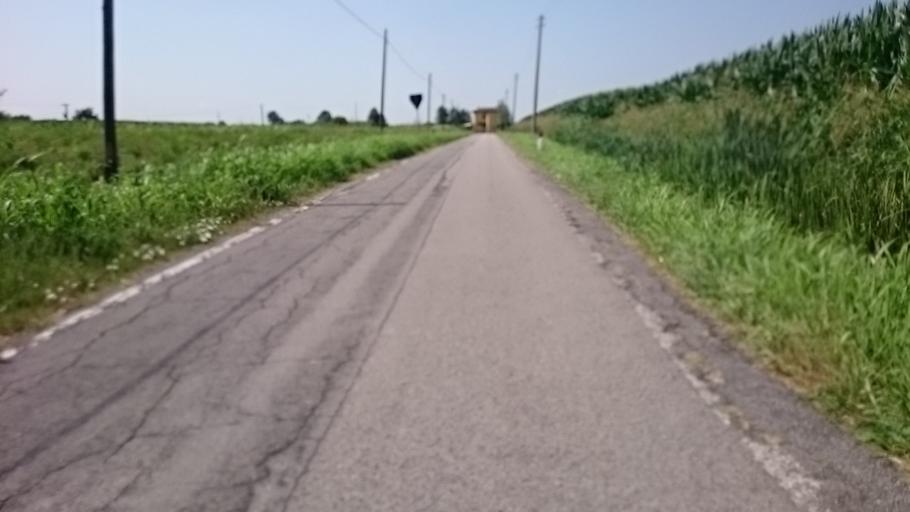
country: IT
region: Veneto
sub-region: Provincia di Padova
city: Masera di Padova
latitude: 45.3298
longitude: 11.8745
